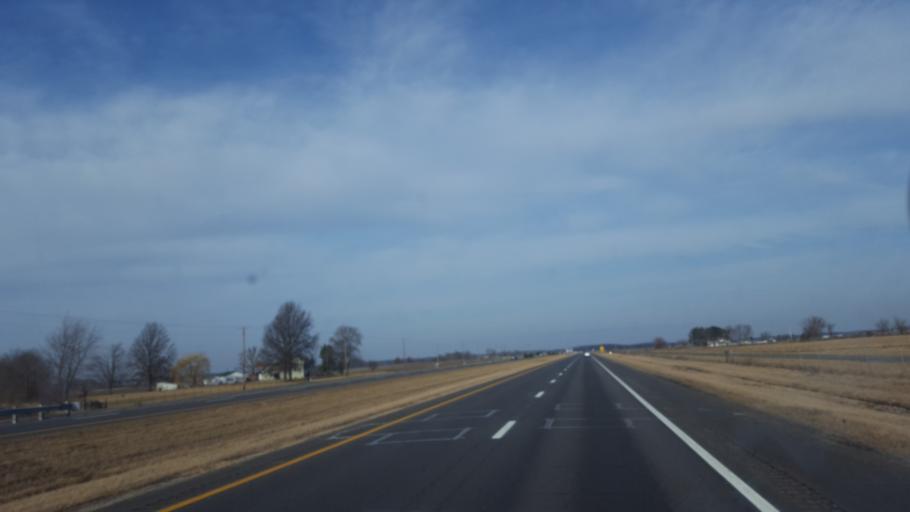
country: US
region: Ohio
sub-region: Marion County
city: Marion
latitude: 40.7121
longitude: -83.1723
